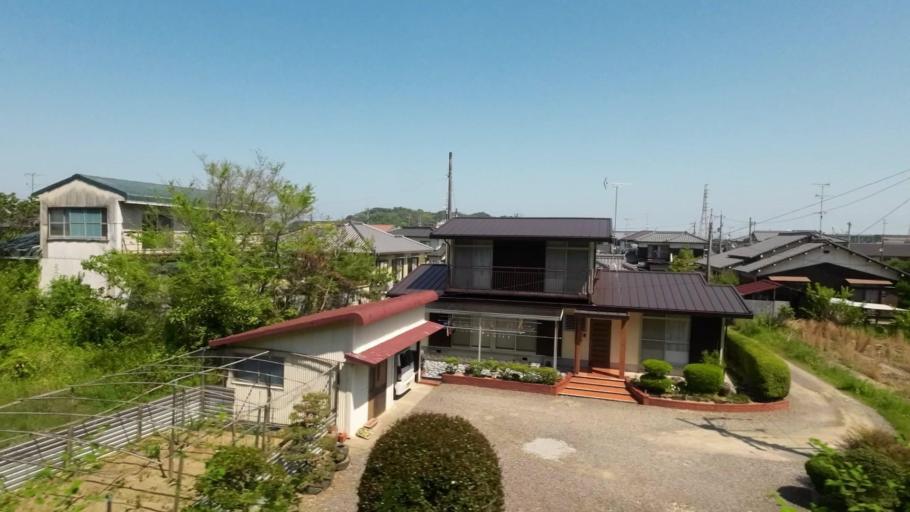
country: JP
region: Ehime
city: Niihama
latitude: 33.9709
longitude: 133.3317
